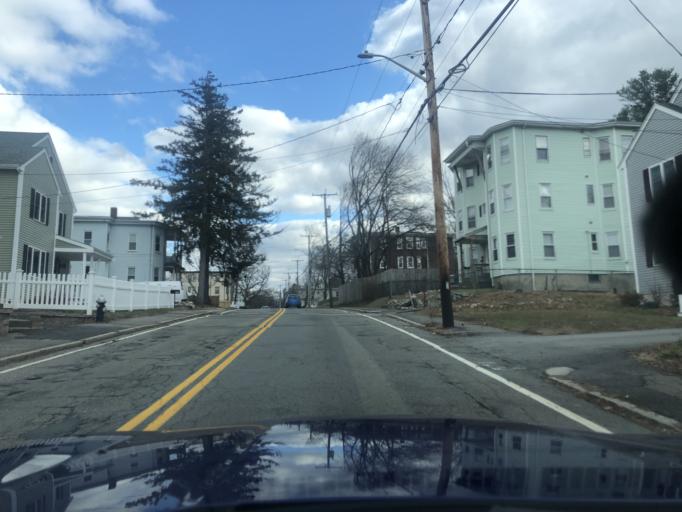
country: US
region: Massachusetts
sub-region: Plymouth County
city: Brockton
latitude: 42.1011
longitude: -71.0119
